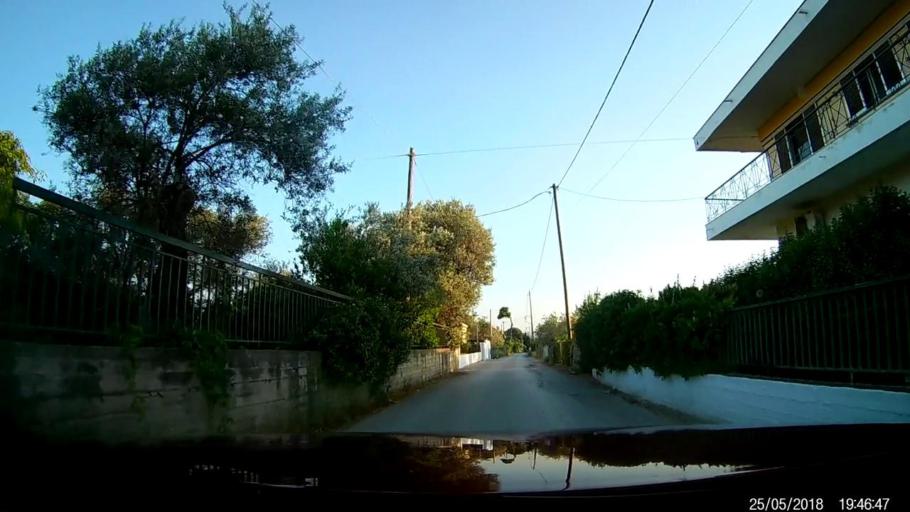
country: GR
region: Central Greece
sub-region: Nomos Evvoias
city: Ayios Nikolaos
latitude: 38.4255
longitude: 23.6409
